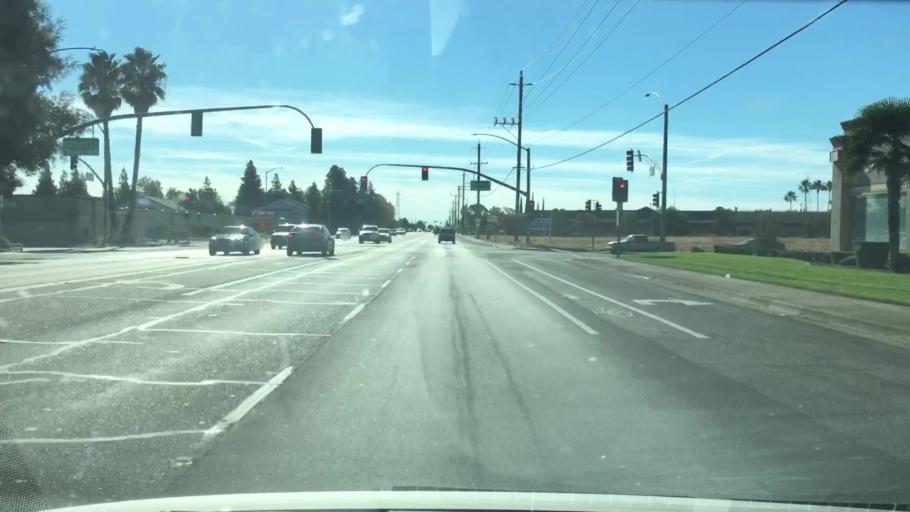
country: US
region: California
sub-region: Sacramento County
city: Florin
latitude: 38.4794
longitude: -121.4214
